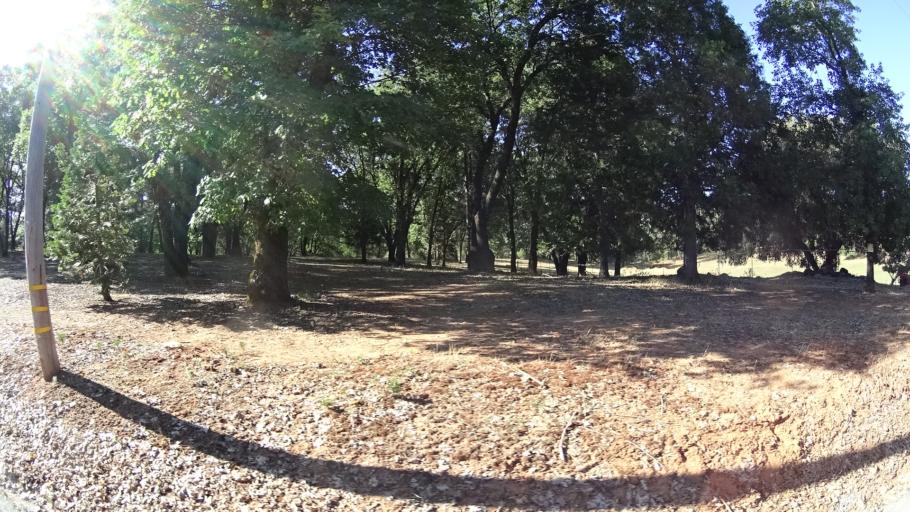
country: US
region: California
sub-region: Amador County
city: Pioneer
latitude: 38.4124
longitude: -120.5534
